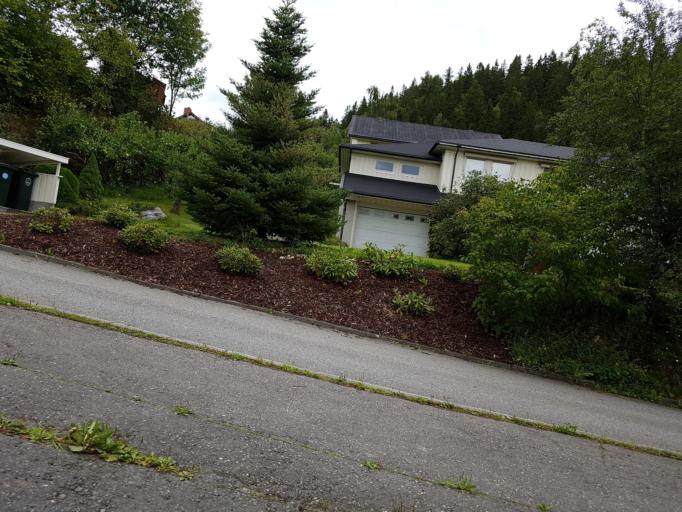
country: NO
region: Sor-Trondelag
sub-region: Trondheim
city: Trondheim
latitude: 63.3977
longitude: 10.4451
